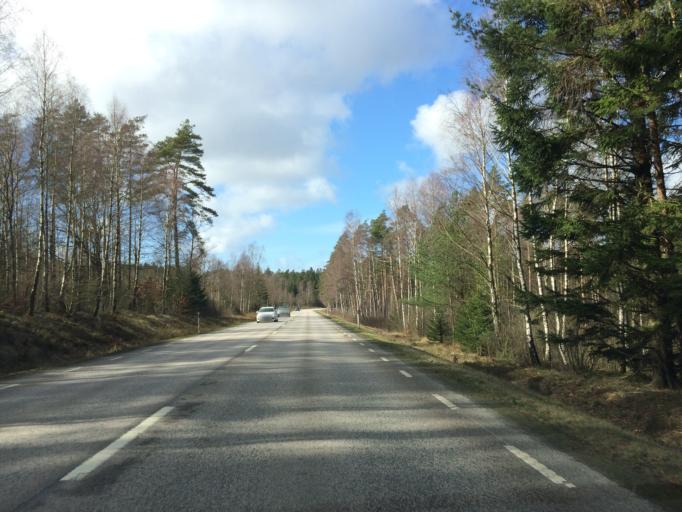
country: SE
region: Halland
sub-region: Laholms Kommun
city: Knared
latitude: 56.4935
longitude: 13.3905
